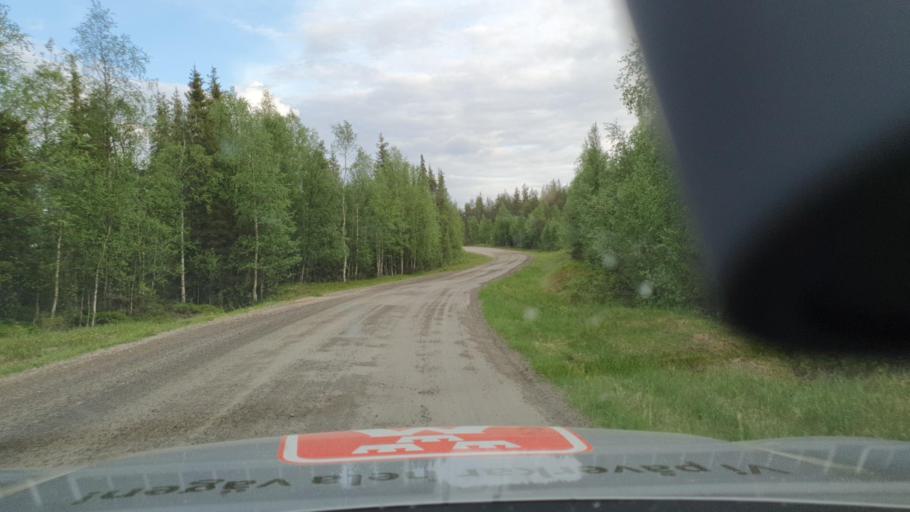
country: SE
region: Norrbotten
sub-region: Gallivare Kommun
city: Gaellivare
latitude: 66.7301
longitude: 21.1427
